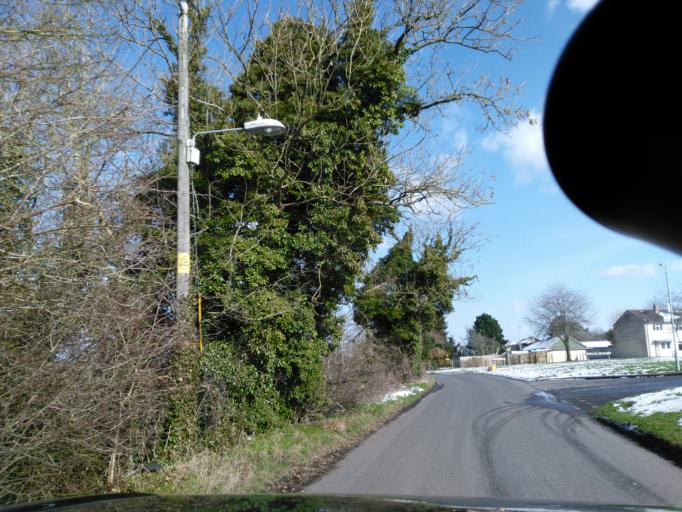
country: GB
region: England
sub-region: Wiltshire
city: Neston
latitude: 51.4220
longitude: -2.2042
